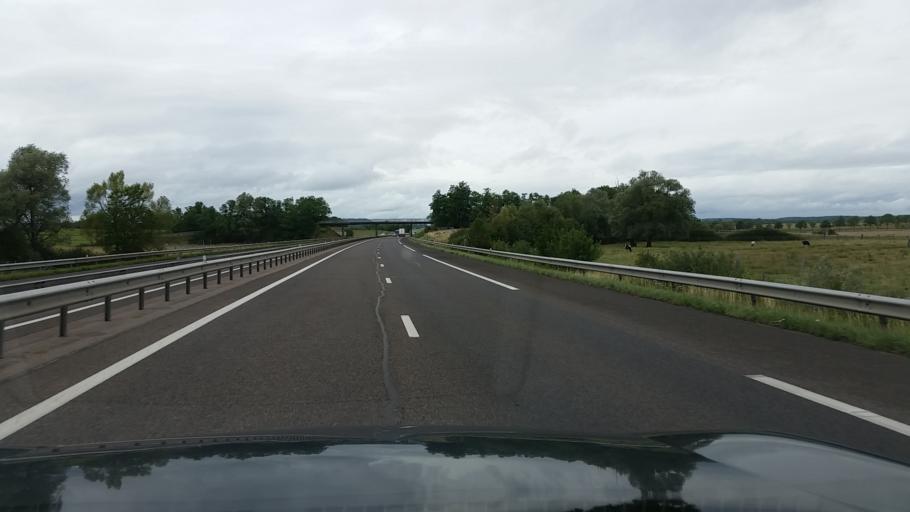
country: FR
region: Lorraine
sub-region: Departement de Meurthe-et-Moselle
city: Blenod-les-Toul
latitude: 48.6037
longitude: 5.8858
